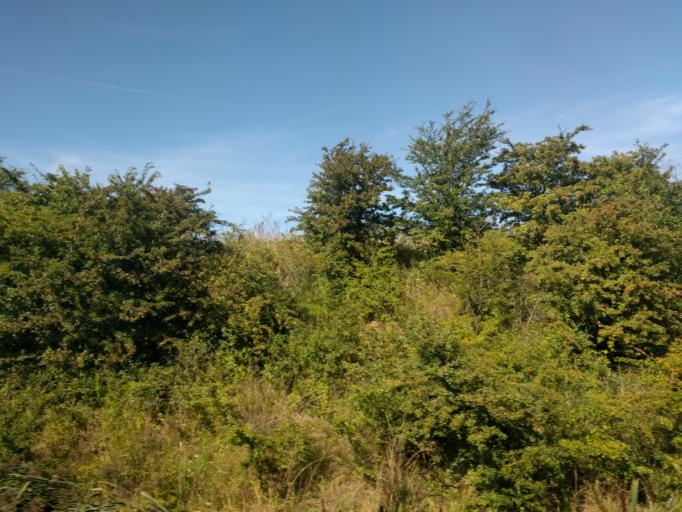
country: DK
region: Zealand
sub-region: Slagelse Kommune
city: Korsor
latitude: 55.3568
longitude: 11.1318
